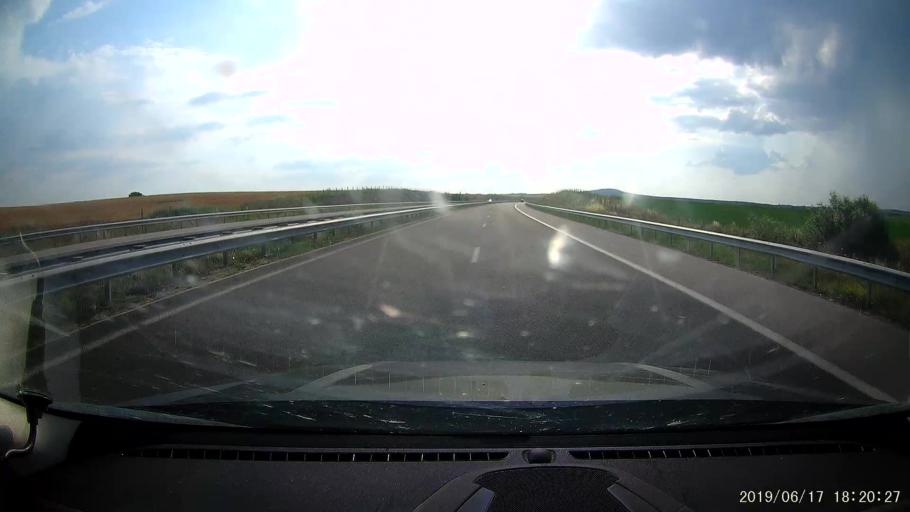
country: BG
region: Khaskovo
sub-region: Obshtina Simeonovgrad
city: Simeonovgrad
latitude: 41.9618
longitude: 25.8135
